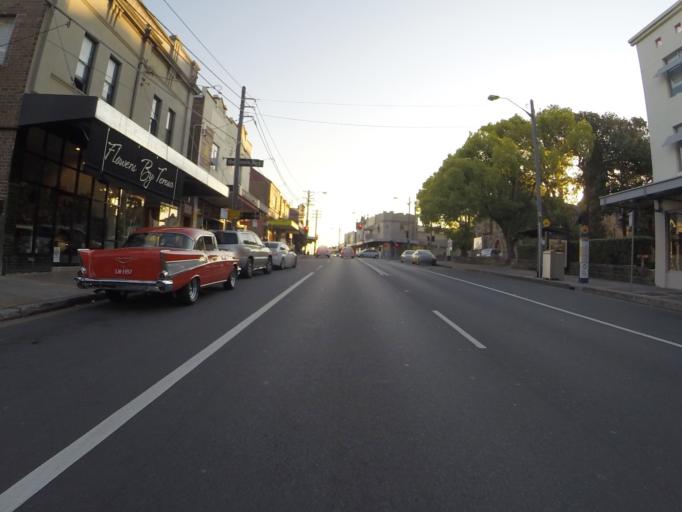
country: AU
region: New South Wales
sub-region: Marrickville
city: Marrickville
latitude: -33.9153
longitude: 151.1511
